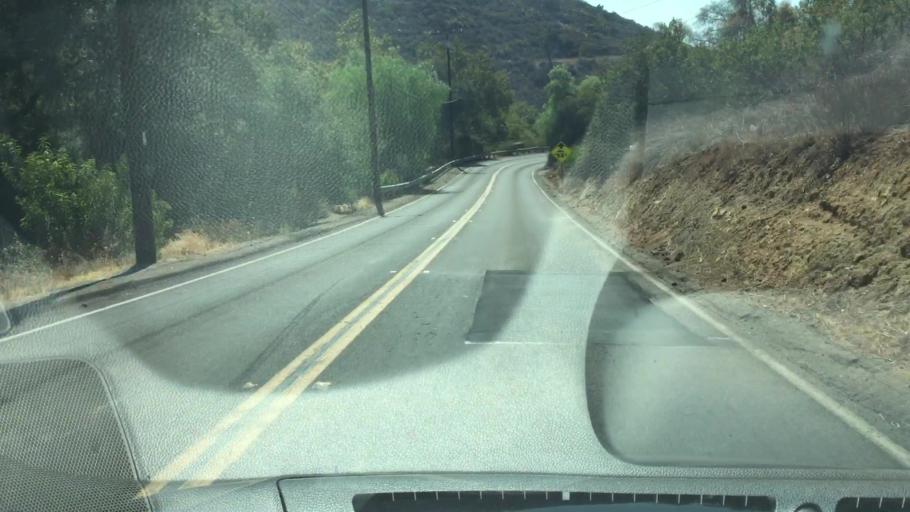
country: US
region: California
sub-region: San Diego County
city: Jamul
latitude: 32.7305
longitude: -116.8766
